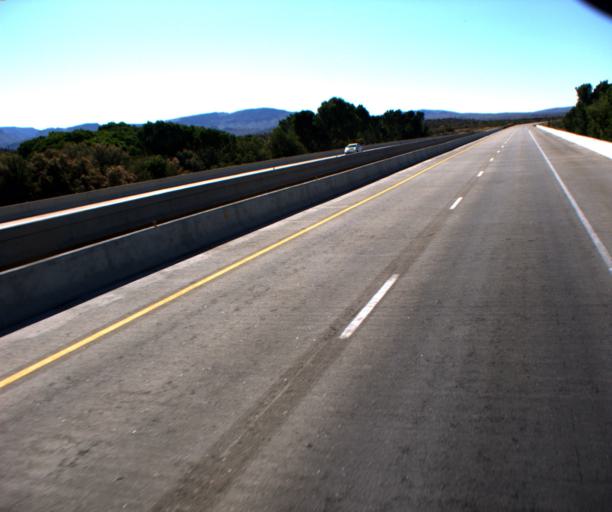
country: US
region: Arizona
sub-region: Yavapai County
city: Bagdad
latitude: 34.6644
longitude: -113.5828
